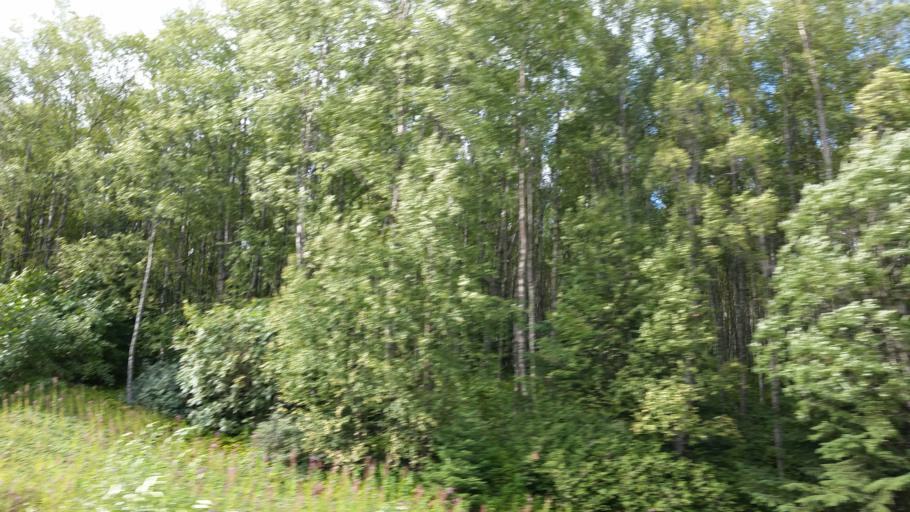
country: US
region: Alaska
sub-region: Anchorage Municipality
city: Girdwood
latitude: 60.9676
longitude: -149.4453
